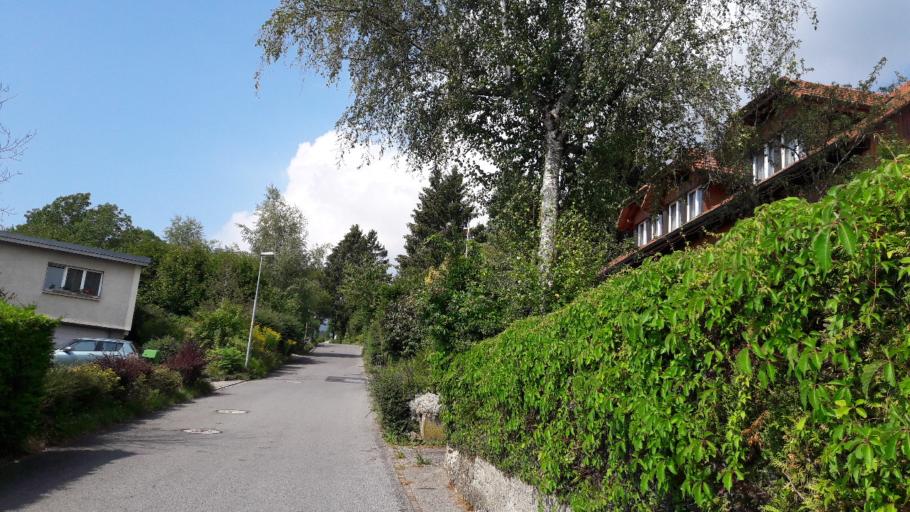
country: CH
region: Solothurn
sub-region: Bezirk Lebern
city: Selzach
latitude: 47.2307
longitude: 7.4714
